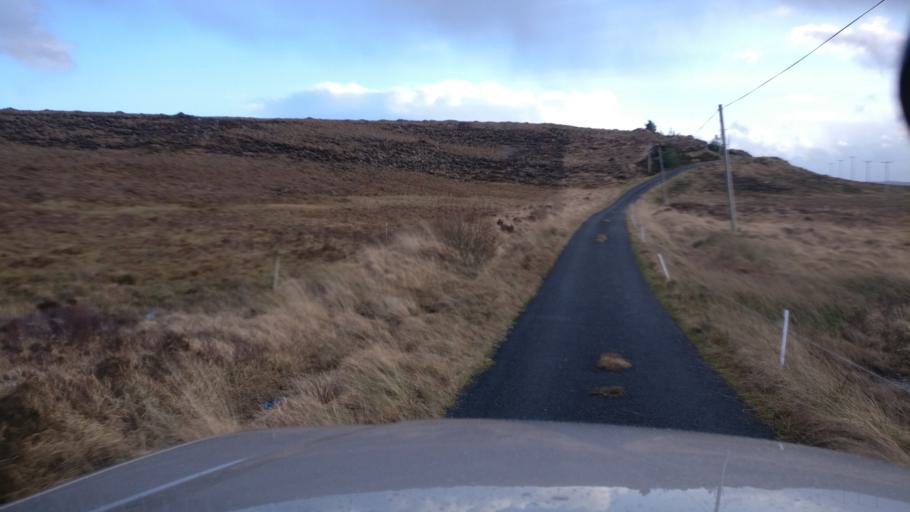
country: IE
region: Connaught
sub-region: County Galway
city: Clifden
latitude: 53.4761
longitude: -9.6925
